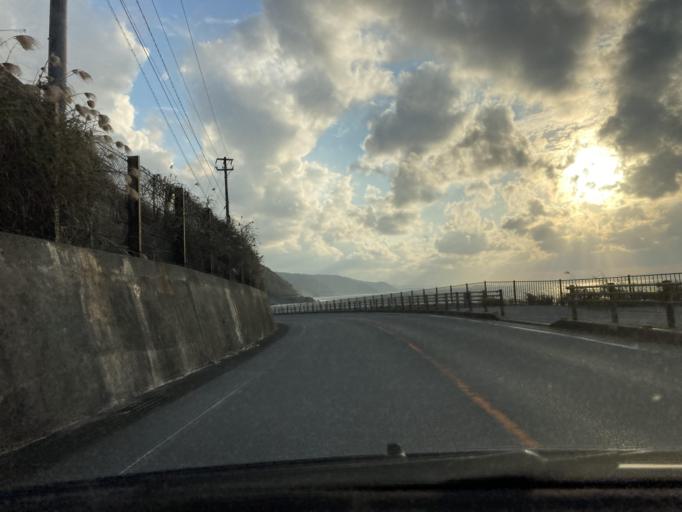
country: JP
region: Okinawa
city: Nago
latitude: 26.8047
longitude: 128.2313
